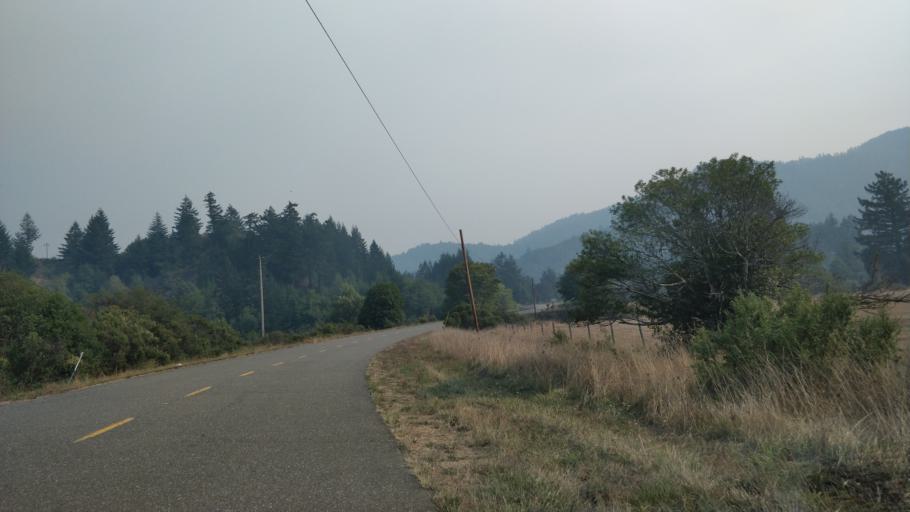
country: US
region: California
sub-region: Humboldt County
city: Rio Dell
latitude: 40.2785
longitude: -124.2444
